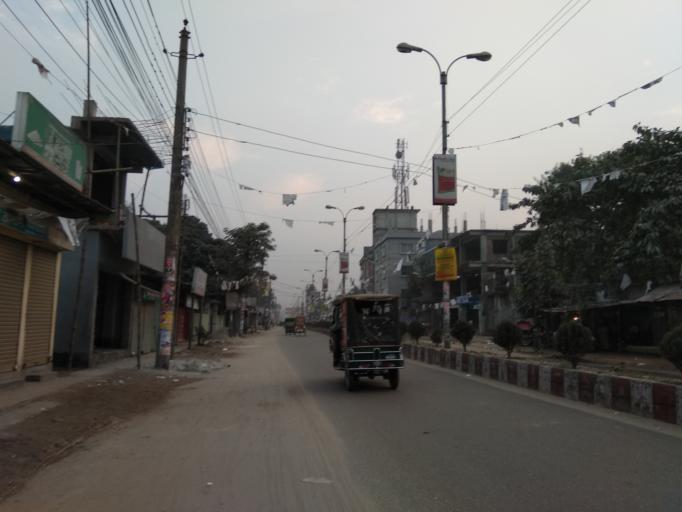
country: BD
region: Rangpur Division
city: Rangpur
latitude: 25.7381
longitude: 89.2548
